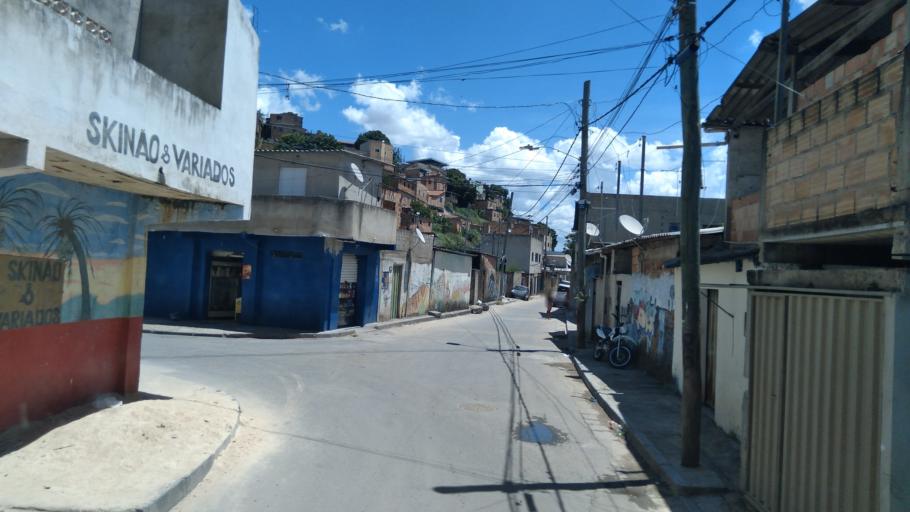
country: BR
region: Minas Gerais
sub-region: Santa Luzia
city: Santa Luzia
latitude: -19.8371
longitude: -43.8958
